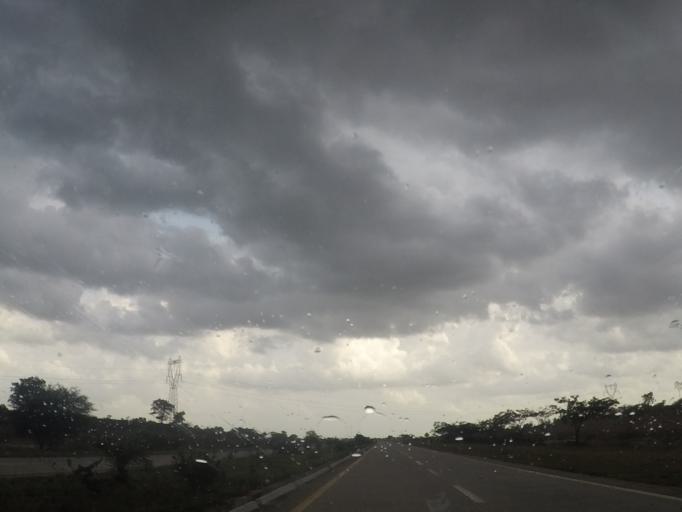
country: MM
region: Mandalay
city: Meiktila
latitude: 20.8895
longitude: 95.7745
